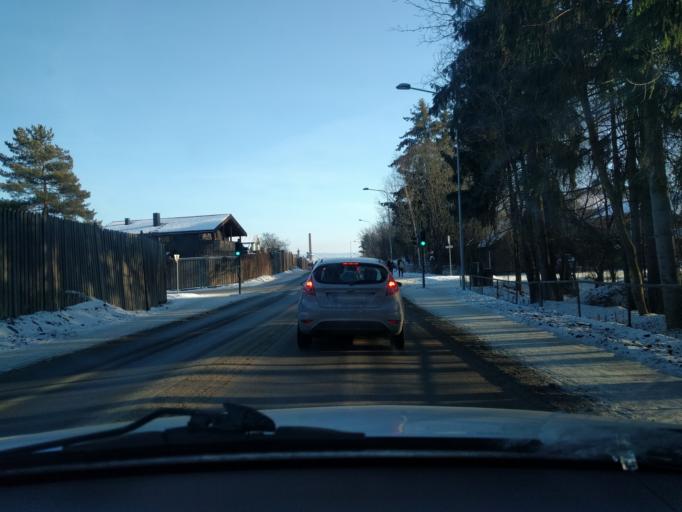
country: NO
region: Hedmark
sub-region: Hamar
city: Hamar
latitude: 60.7969
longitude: 11.0532
